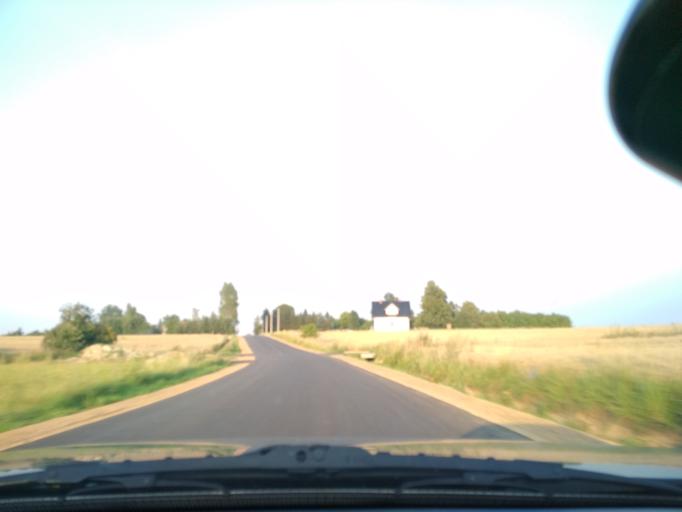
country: PL
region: Lesser Poland Voivodeship
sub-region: Powiat olkuski
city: Wolbrom
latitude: 50.4072
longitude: 19.8081
